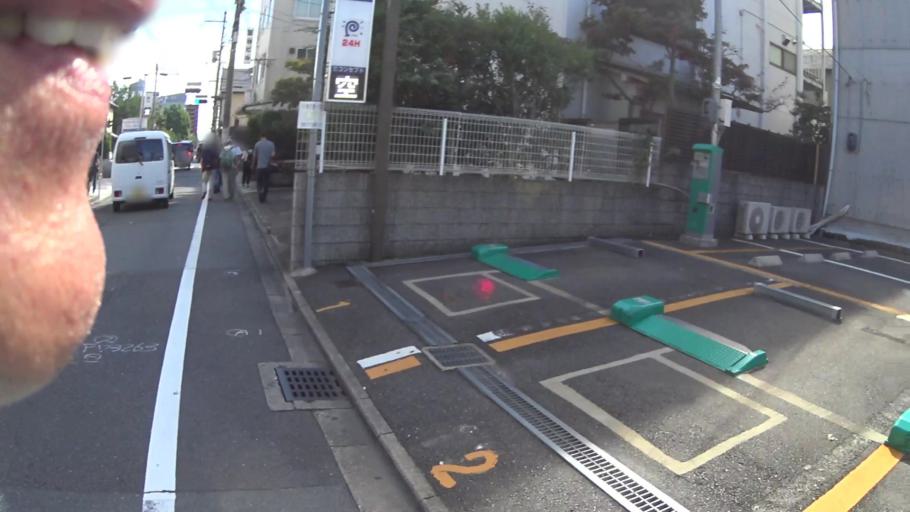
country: JP
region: Kyoto
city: Kyoto
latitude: 34.9992
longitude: 135.7427
